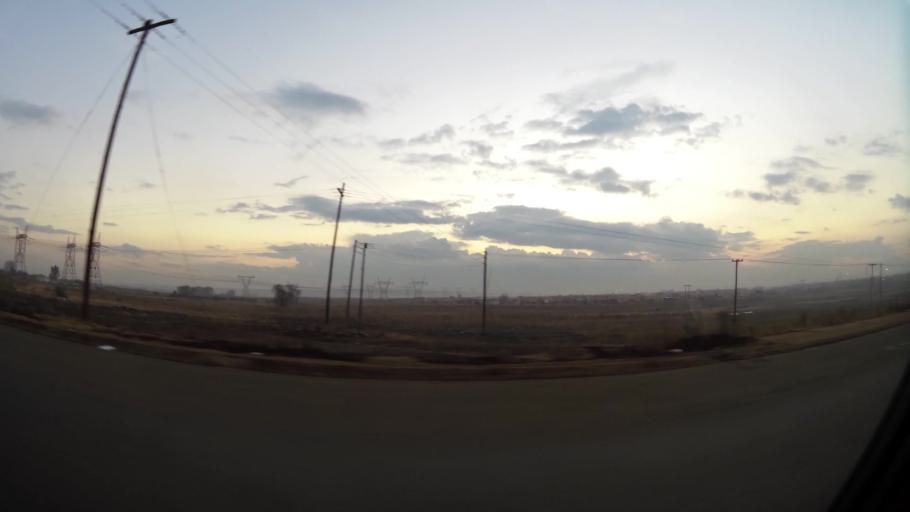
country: ZA
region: Gauteng
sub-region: City of Johannesburg Metropolitan Municipality
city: Orange Farm
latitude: -26.5493
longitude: 27.8307
